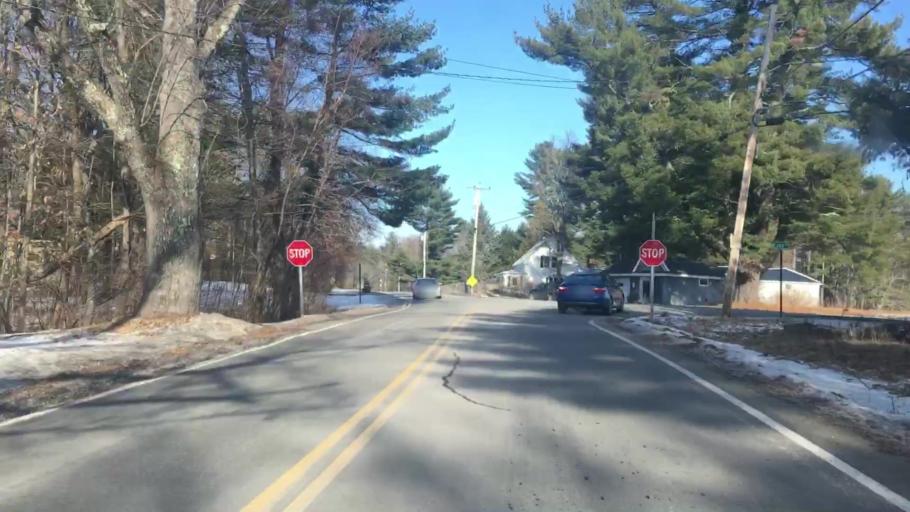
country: US
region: Maine
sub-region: Androscoggin County
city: Auburn
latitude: 44.1190
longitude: -70.2704
